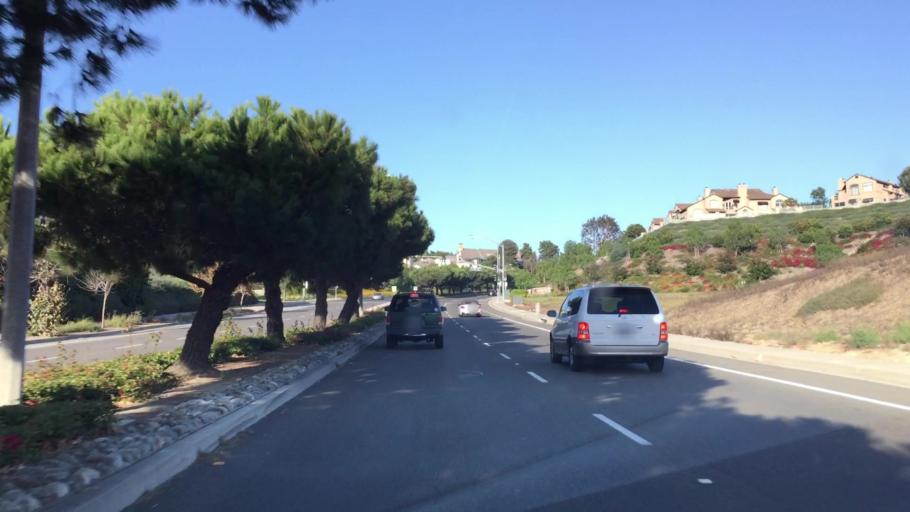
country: US
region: California
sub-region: Orange County
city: Dana Point
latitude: 33.4901
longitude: -117.7040
